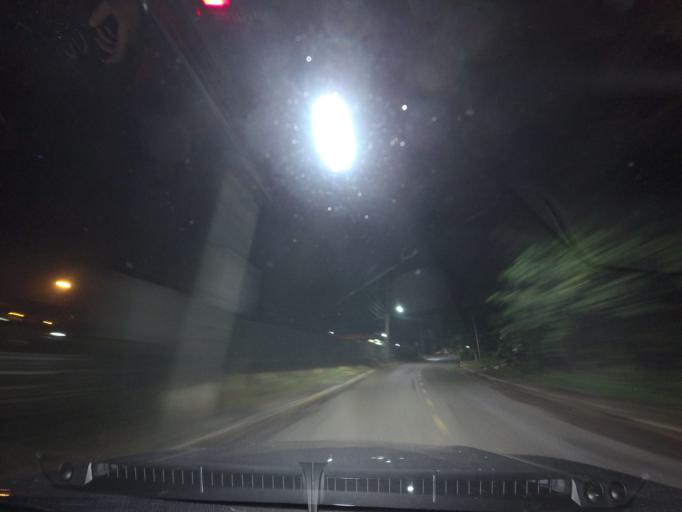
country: TH
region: Nong Khai
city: Nong Khai
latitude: 17.8640
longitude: 102.7224
